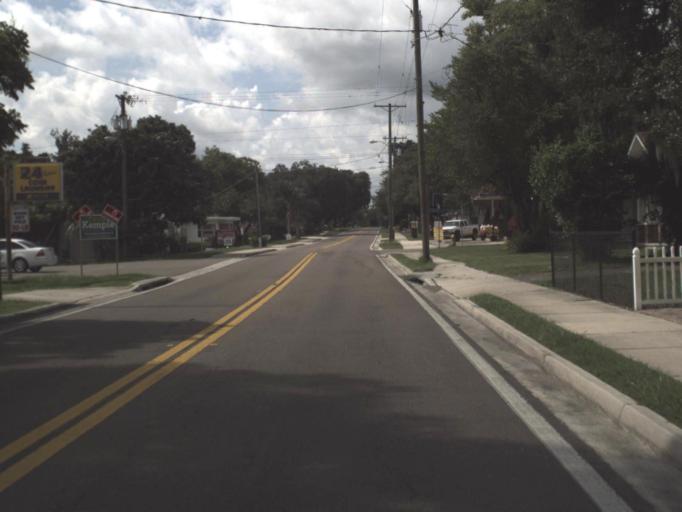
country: US
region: Florida
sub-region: Hillsborough County
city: Plant City
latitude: 28.0259
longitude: -82.1257
